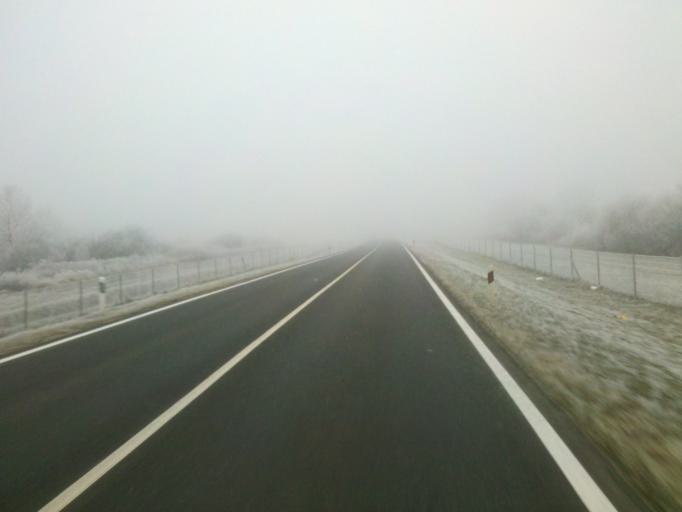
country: HR
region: Varazdinska
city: Jalkovec
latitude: 46.2678
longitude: 16.3448
